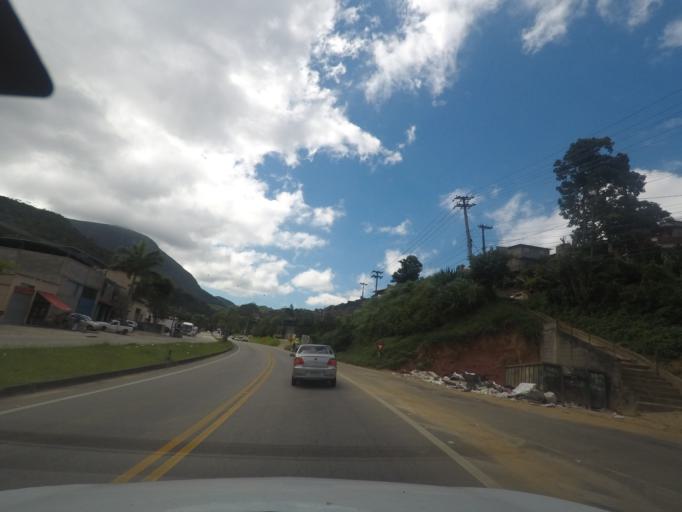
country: BR
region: Rio de Janeiro
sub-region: Teresopolis
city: Teresopolis
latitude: -22.3994
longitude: -42.9550
